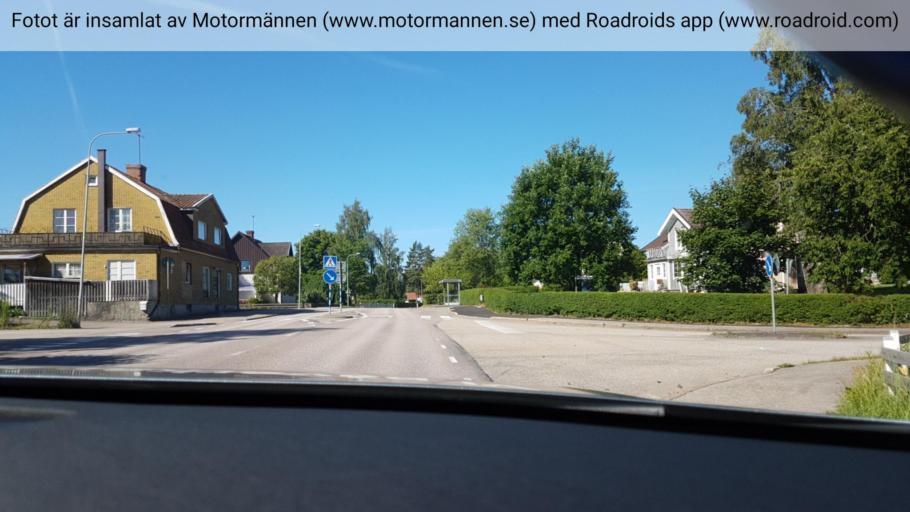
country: SE
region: Vaestra Goetaland
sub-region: Ulricehamns Kommun
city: Ulricehamn
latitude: 57.8986
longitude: 13.4658
